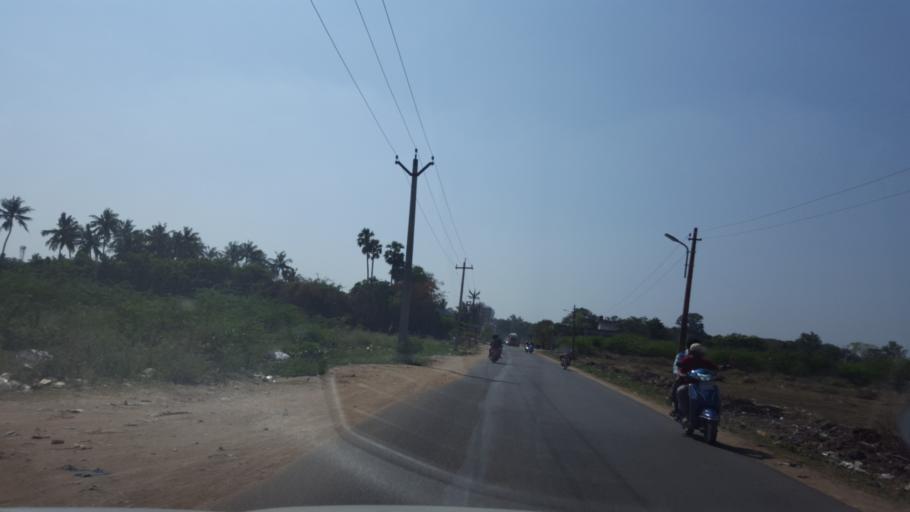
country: IN
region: Tamil Nadu
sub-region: Kancheepuram
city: Kanchipuram
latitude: 12.8391
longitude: 79.7177
